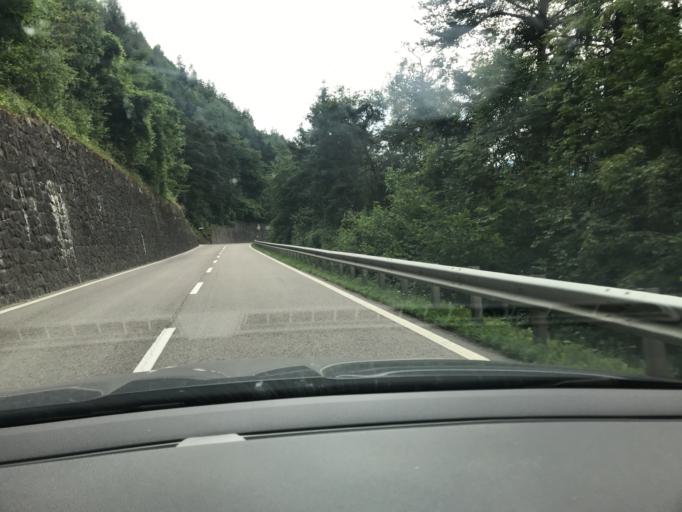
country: IT
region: Trentino-Alto Adige
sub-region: Bolzano
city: Chiusa
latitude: 46.6318
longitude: 11.5587
